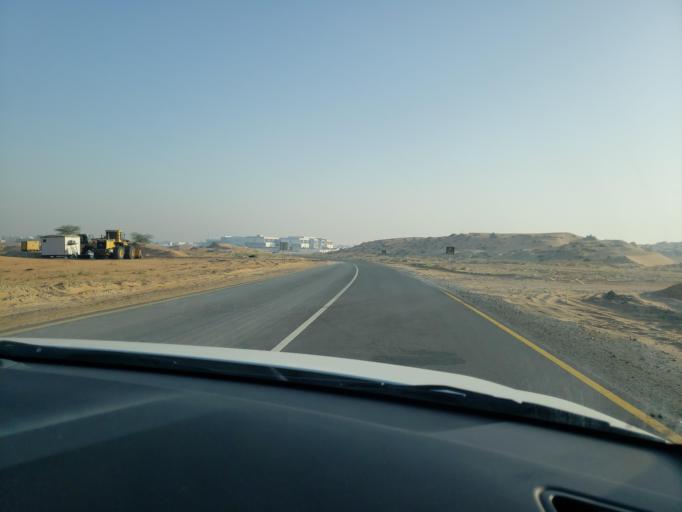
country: AE
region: Umm al Qaywayn
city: Umm al Qaywayn
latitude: 25.4627
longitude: 55.6101
